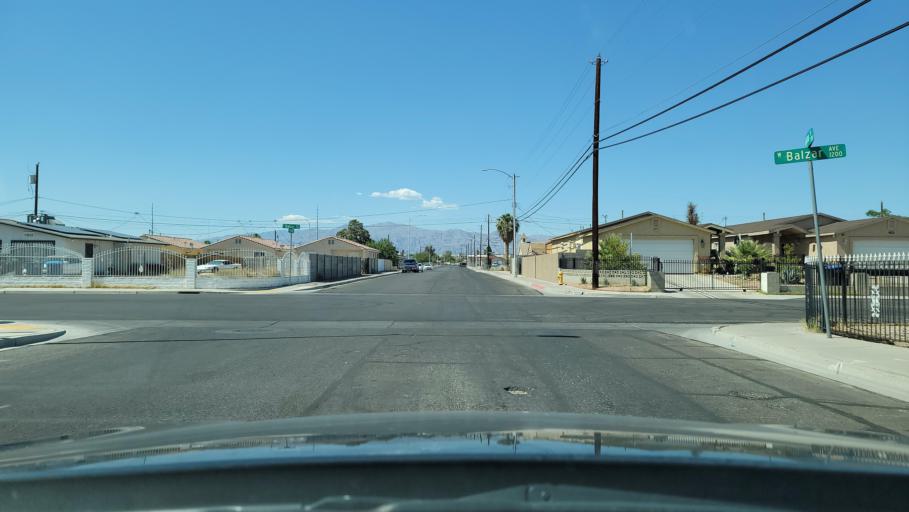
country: US
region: Nevada
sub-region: Clark County
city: Las Vegas
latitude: 36.1991
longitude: -115.1585
